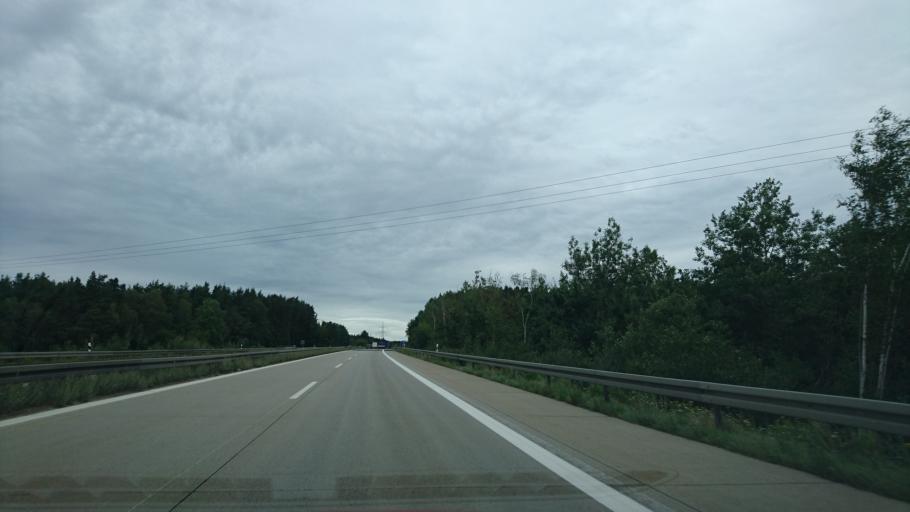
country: DE
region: Bavaria
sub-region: Upper Palatinate
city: Luhe-Wildenau
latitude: 49.5656
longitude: 12.1218
